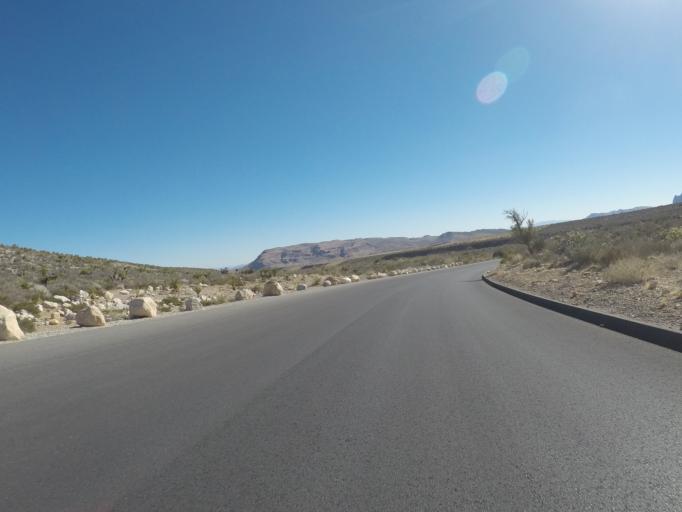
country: US
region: Nevada
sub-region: Clark County
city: Summerlin South
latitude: 36.1466
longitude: -115.4768
